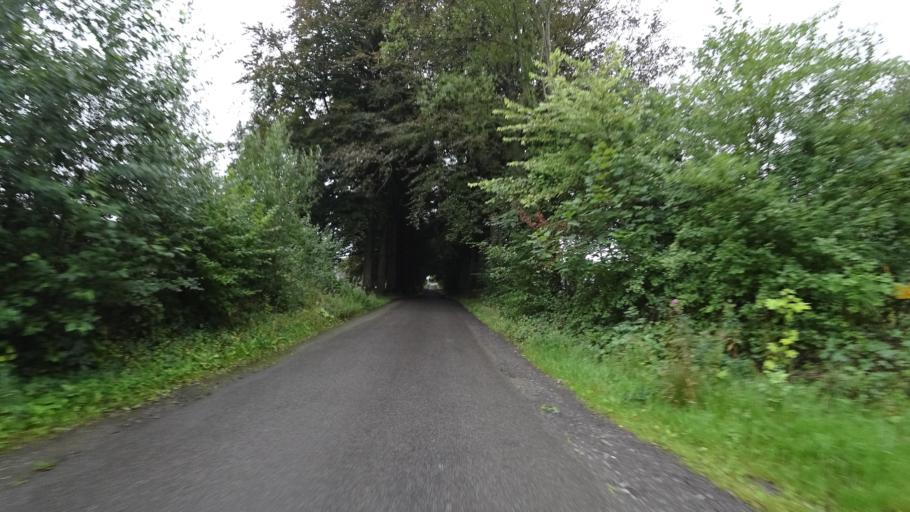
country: BE
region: Wallonia
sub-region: Province de Namur
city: Namur
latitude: 50.4941
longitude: 4.8092
